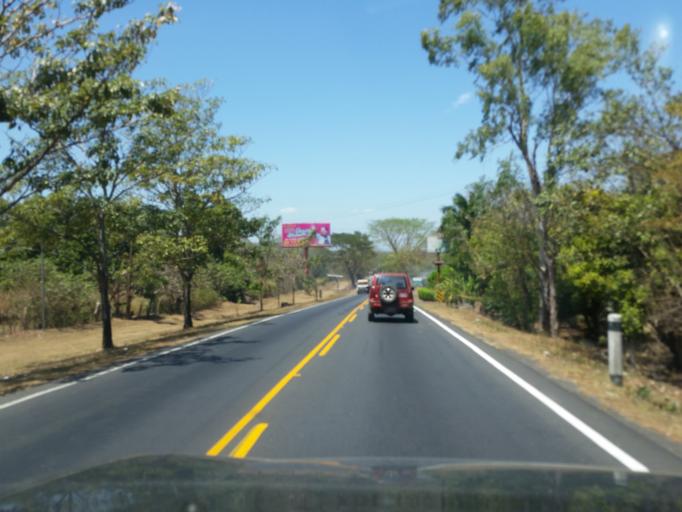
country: NI
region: Masaya
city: Masaya
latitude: 11.9506
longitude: -86.0918
